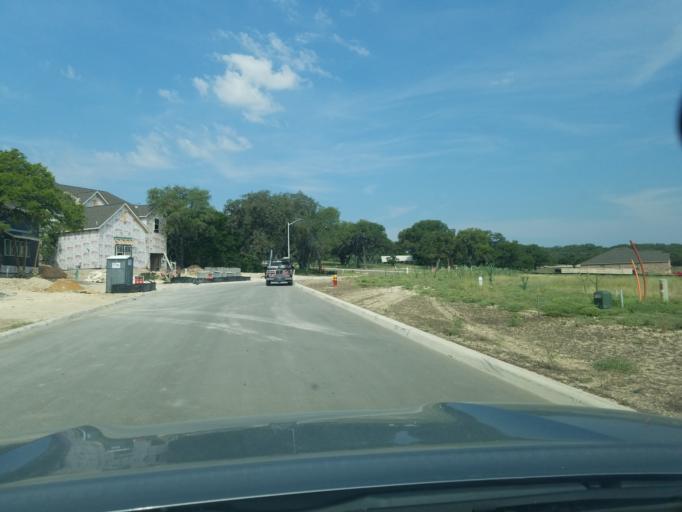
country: US
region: Texas
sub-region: Kendall County
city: Boerne
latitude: 29.7518
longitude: -98.7154
